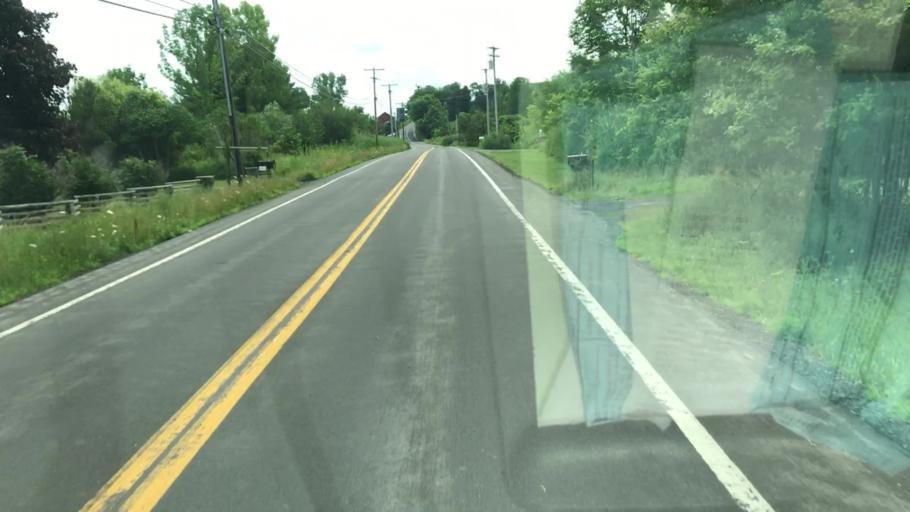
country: US
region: New York
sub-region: Onondaga County
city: Manlius
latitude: 42.9660
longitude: -75.9872
